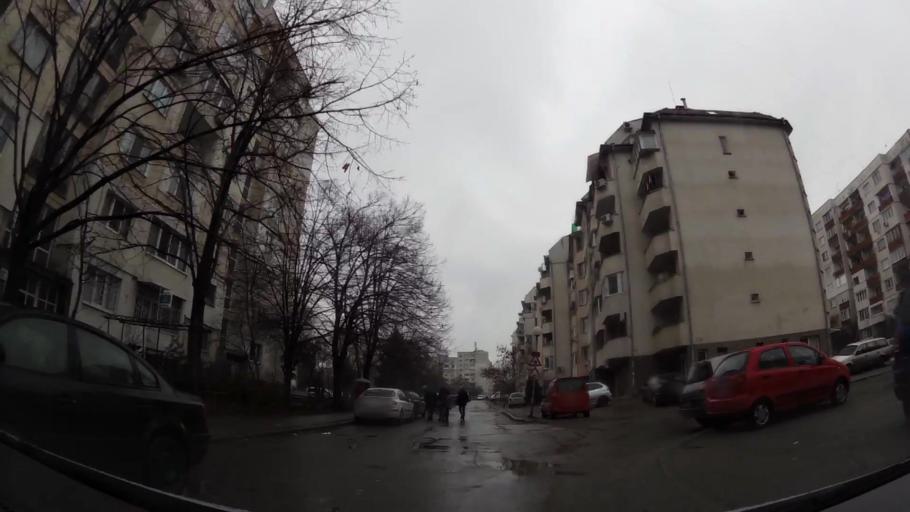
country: BG
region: Sofia-Capital
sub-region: Stolichna Obshtina
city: Sofia
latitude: 42.6397
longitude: 23.3760
